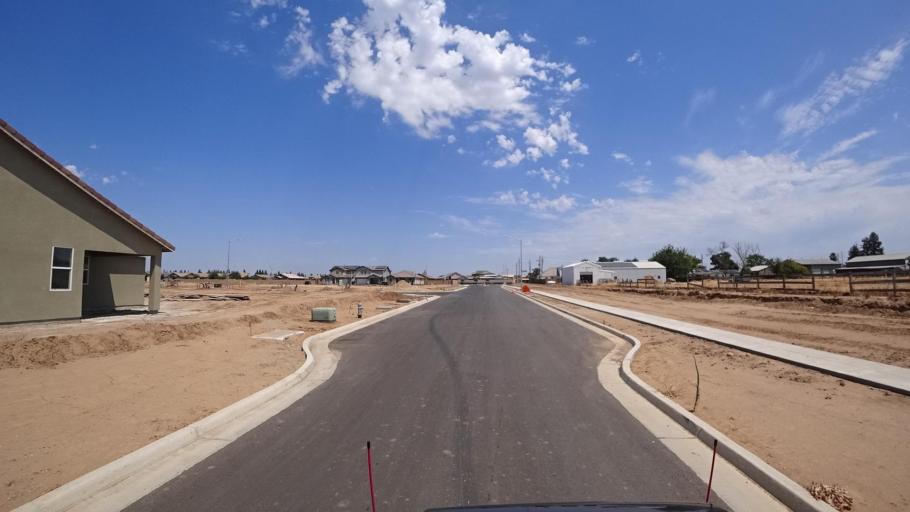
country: US
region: California
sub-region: Fresno County
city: Sunnyside
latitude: 36.7705
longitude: -119.6778
